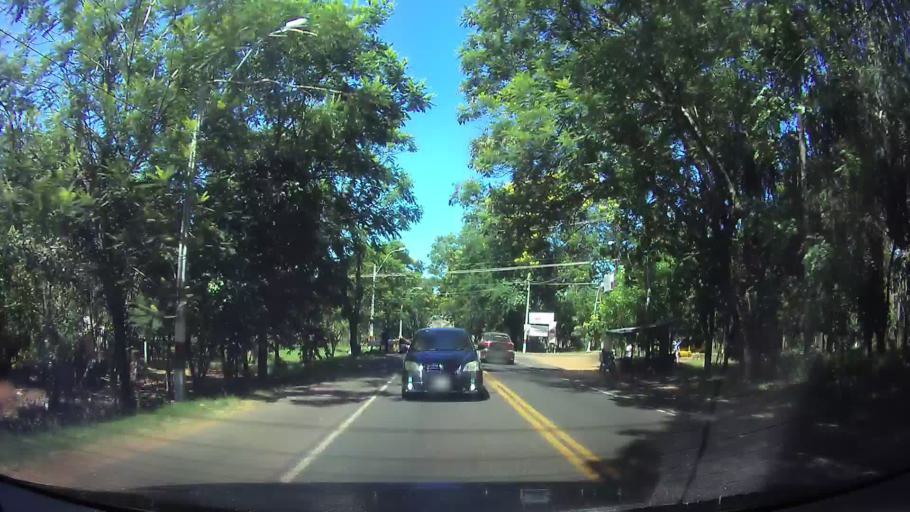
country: PY
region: Central
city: Aregua
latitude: -25.3226
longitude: -57.3916
